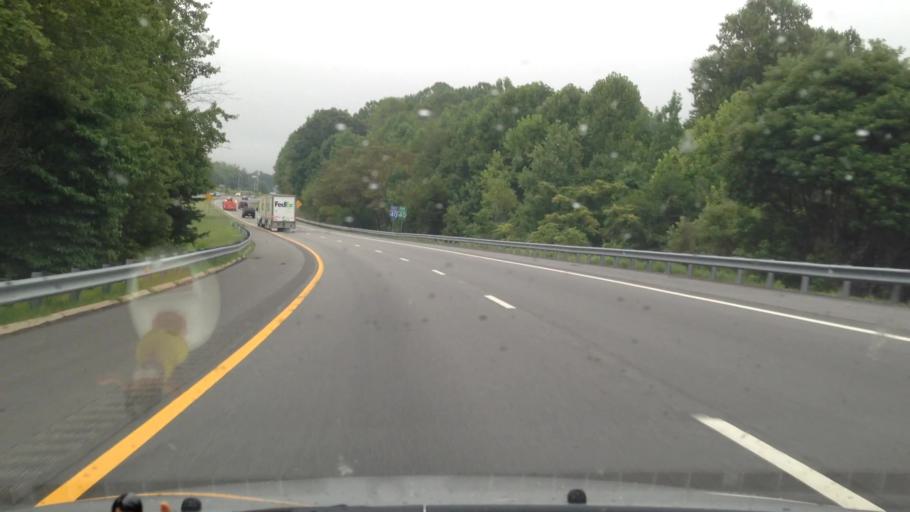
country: US
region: North Carolina
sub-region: Forsyth County
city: Kernersville
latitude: 36.0963
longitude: -80.0133
